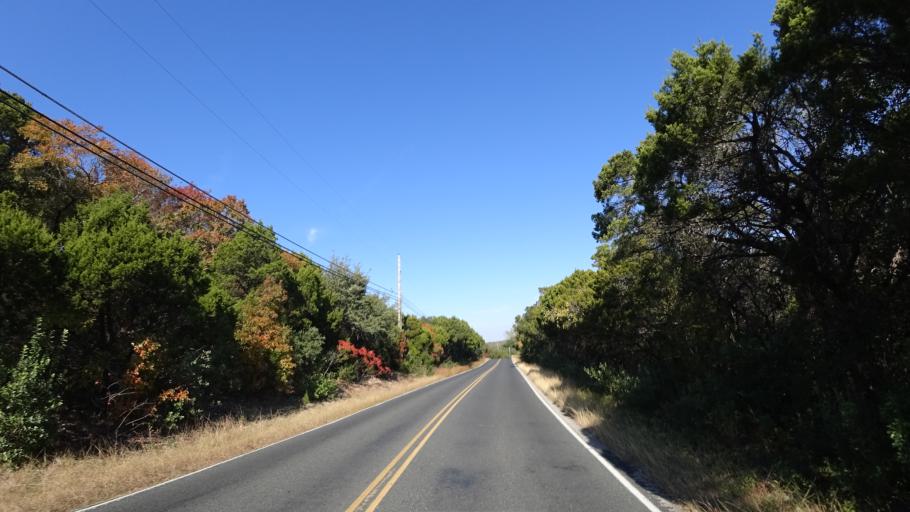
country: US
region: Texas
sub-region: Williamson County
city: Jollyville
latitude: 30.3871
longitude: -97.7732
